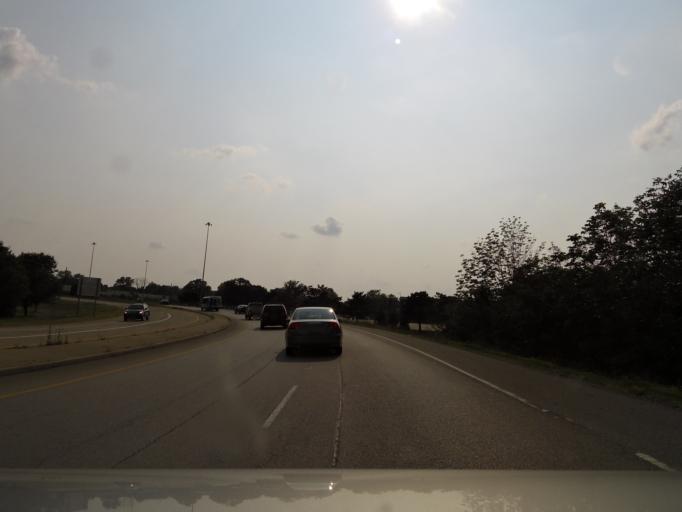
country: US
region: Ohio
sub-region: Hamilton County
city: Springdale
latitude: 39.2969
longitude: -84.4669
